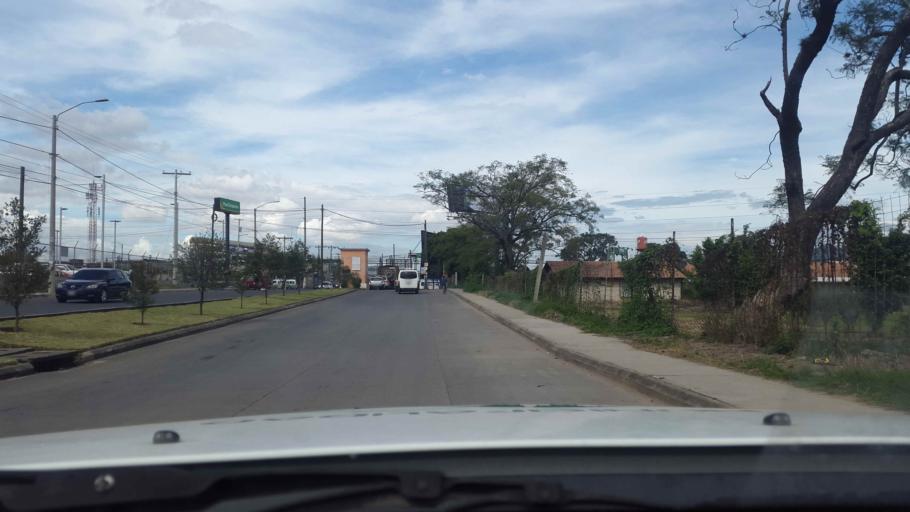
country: GT
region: Guatemala
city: Petapa
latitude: 14.5075
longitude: -90.5705
